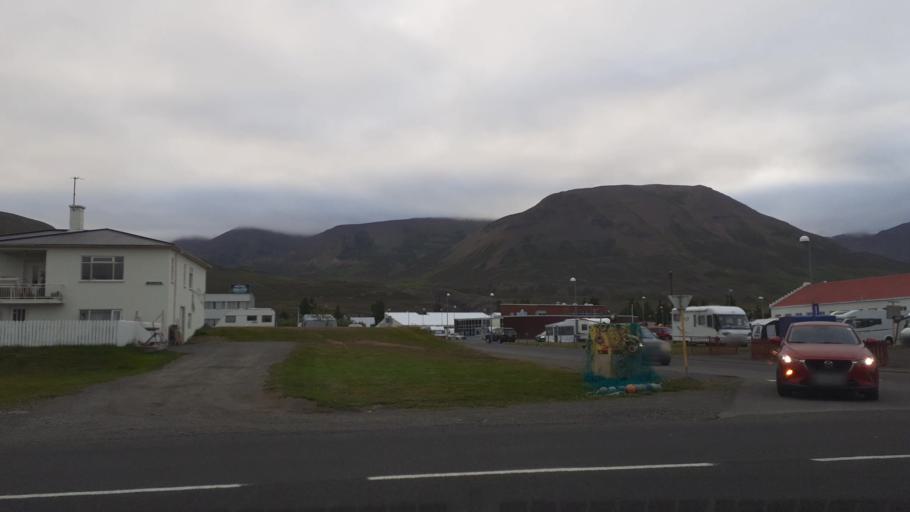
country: IS
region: Northeast
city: Dalvik
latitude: 65.9674
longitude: -18.5296
